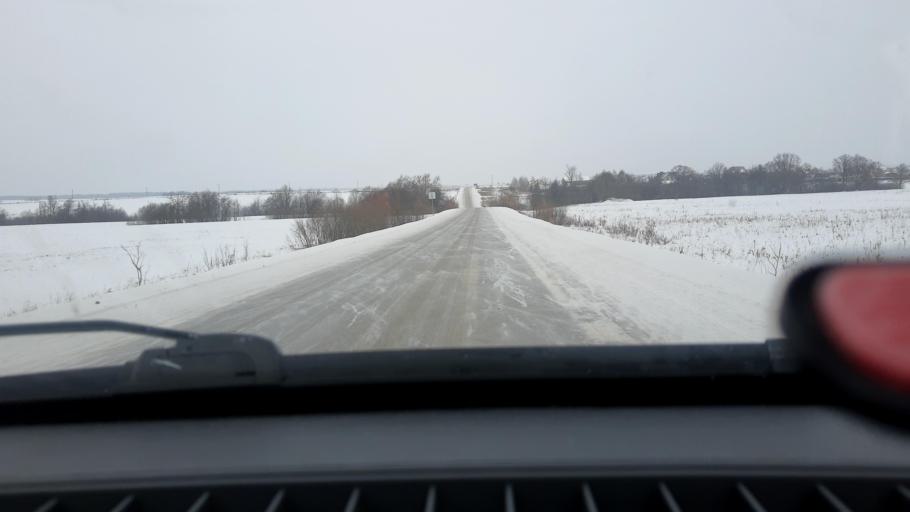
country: RU
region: Bashkortostan
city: Iglino
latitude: 54.7045
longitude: 56.4071
